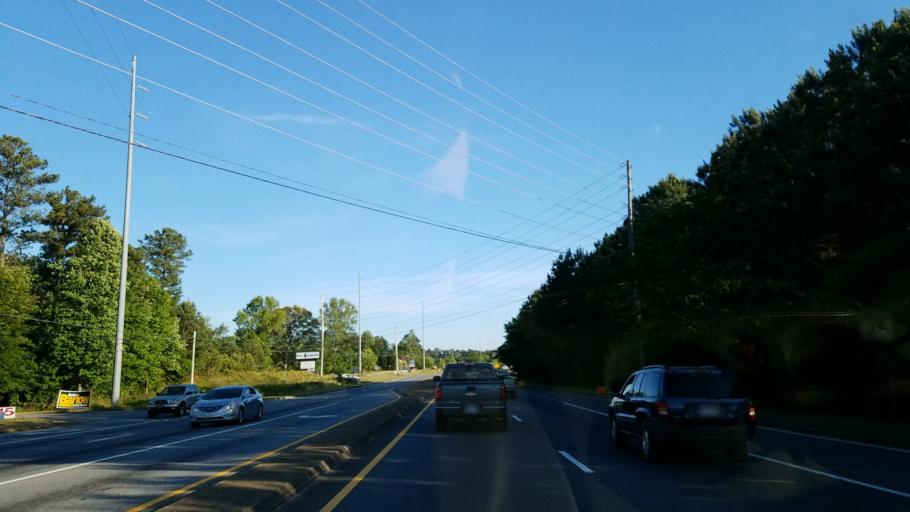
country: US
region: Georgia
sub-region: Cherokee County
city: Woodstock
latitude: 34.1117
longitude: -84.5819
